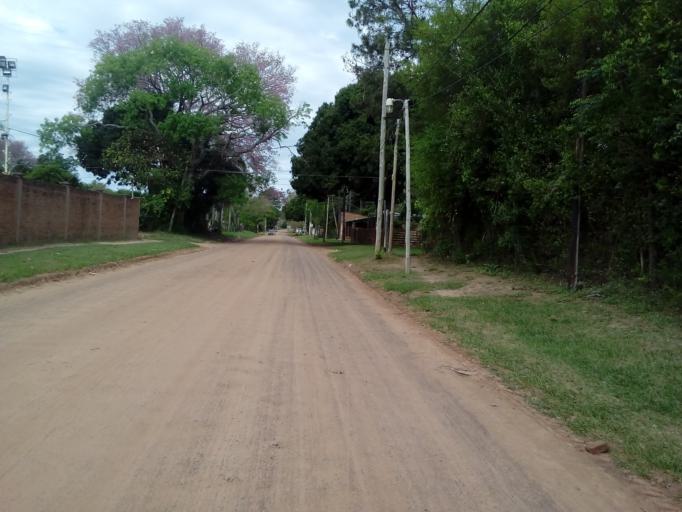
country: AR
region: Corrientes
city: San Luis del Palmar
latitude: -27.4577
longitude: -58.6577
